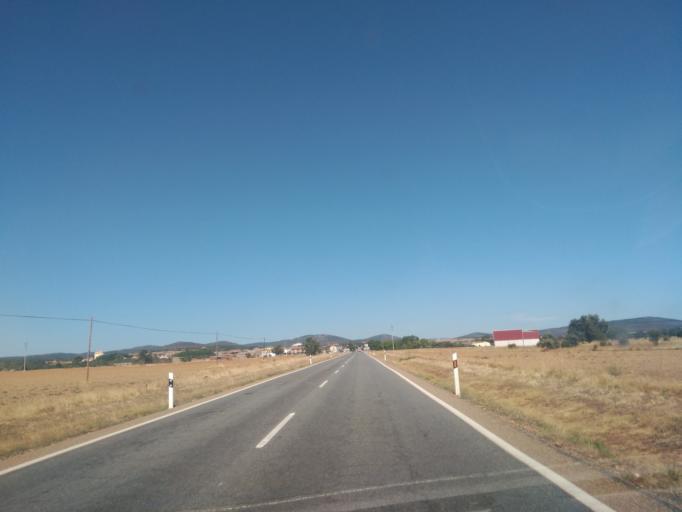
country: ES
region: Castille and Leon
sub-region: Provincia de Zamora
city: Tabara
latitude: 41.8172
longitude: -5.9443
